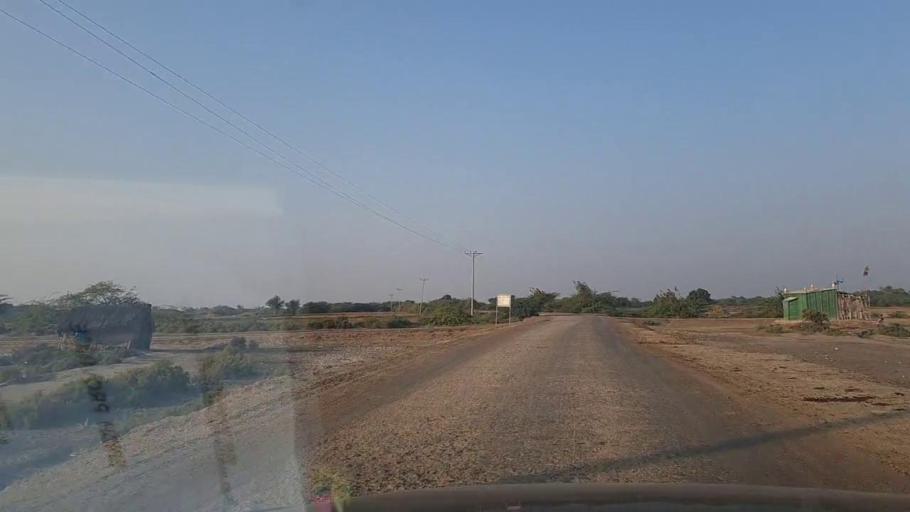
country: PK
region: Sindh
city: Keti Bandar
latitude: 24.2827
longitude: 67.5876
